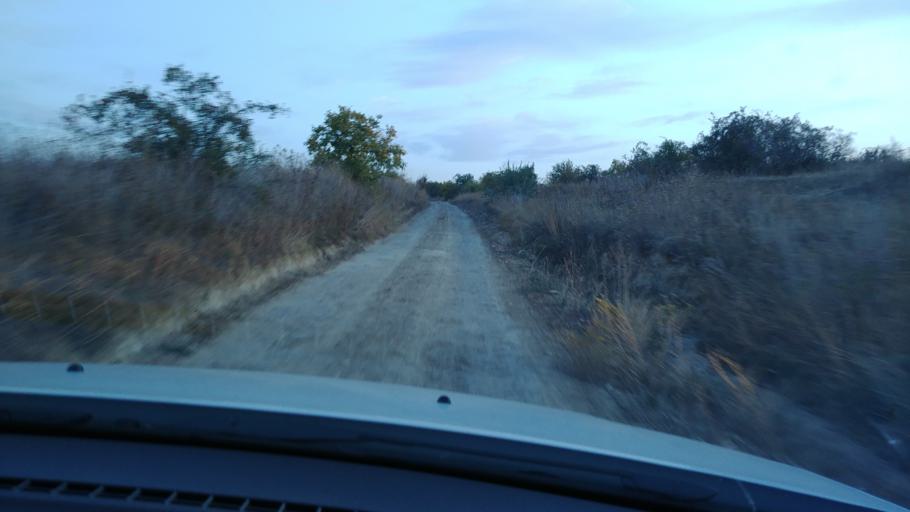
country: MD
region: Rezina
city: Saharna
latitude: 47.6848
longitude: 28.9079
